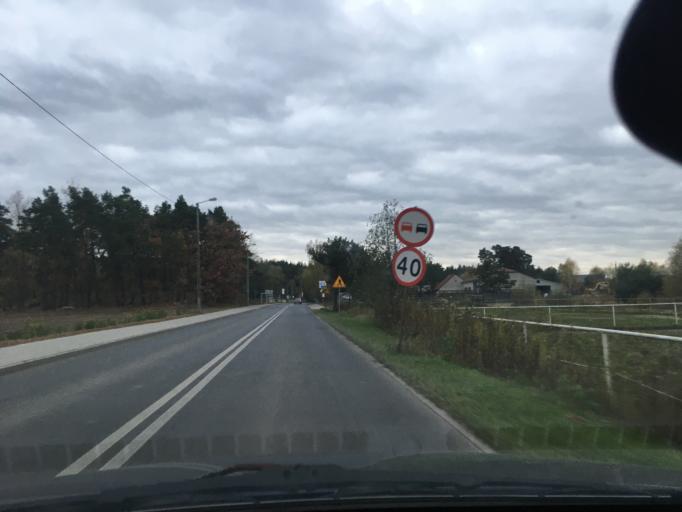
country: PL
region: Masovian Voivodeship
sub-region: Powiat piaseczynski
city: Lesznowola
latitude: 52.0690
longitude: 20.9343
